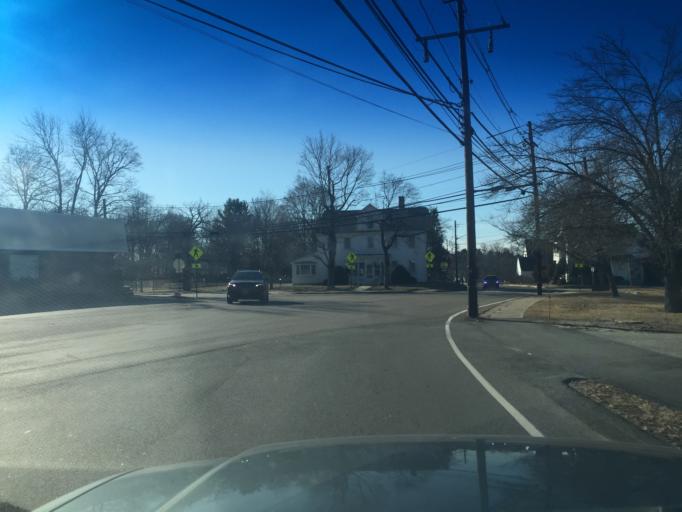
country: US
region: Massachusetts
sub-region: Norfolk County
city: Millis
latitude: 42.1701
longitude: -71.3597
